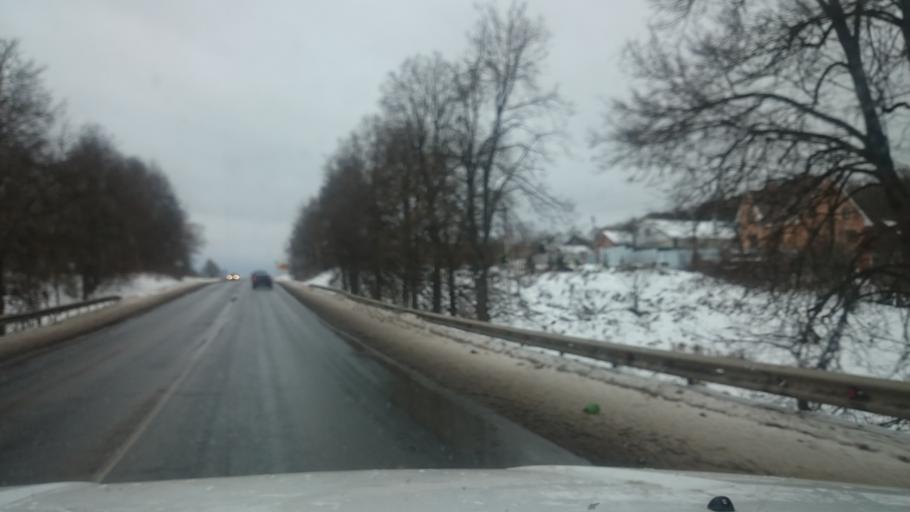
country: RU
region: Tula
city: Kosaya Gora
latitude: 54.1069
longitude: 37.5538
